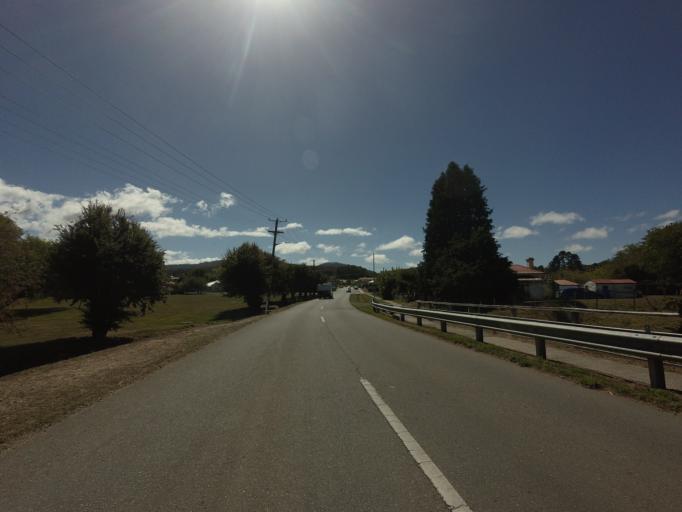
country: AU
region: Tasmania
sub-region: Break O'Day
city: St Helens
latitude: -41.5823
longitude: 148.1853
